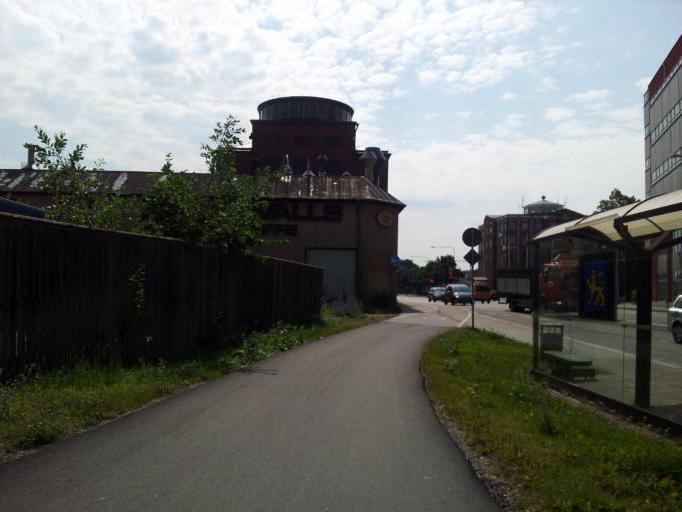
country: SE
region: Uppsala
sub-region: Uppsala Kommun
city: Uppsala
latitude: 59.8553
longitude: 17.6501
